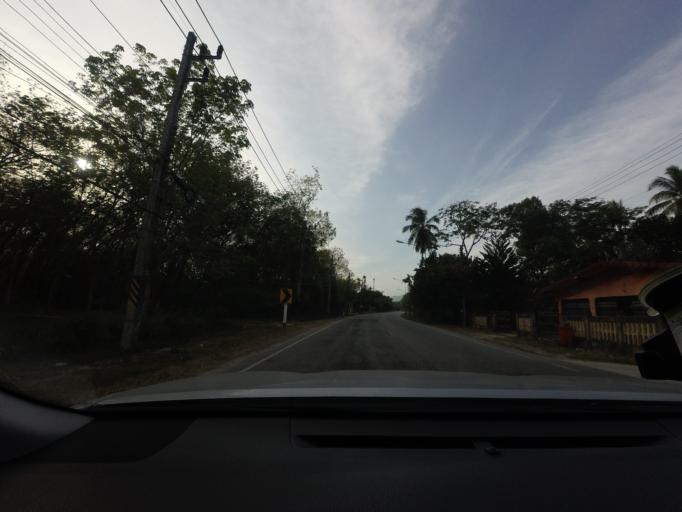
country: TH
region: Narathiwat
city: Ra-ngae
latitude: 6.3427
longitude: 101.7031
